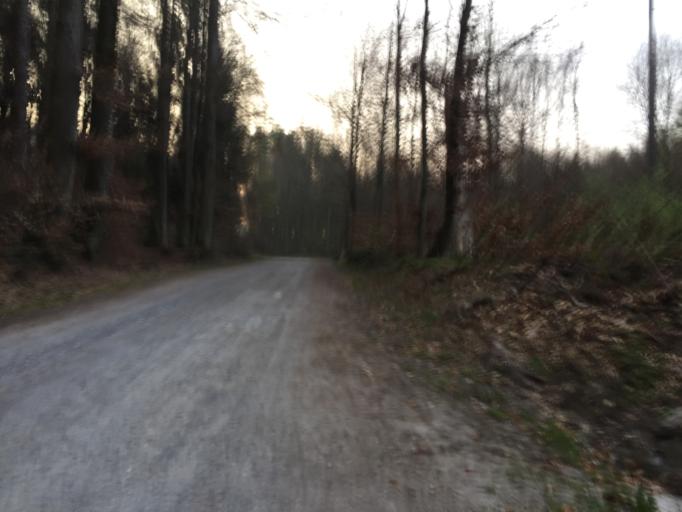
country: CH
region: Bern
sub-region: Bern-Mittelland District
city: Koniz
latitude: 46.9182
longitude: 7.4277
